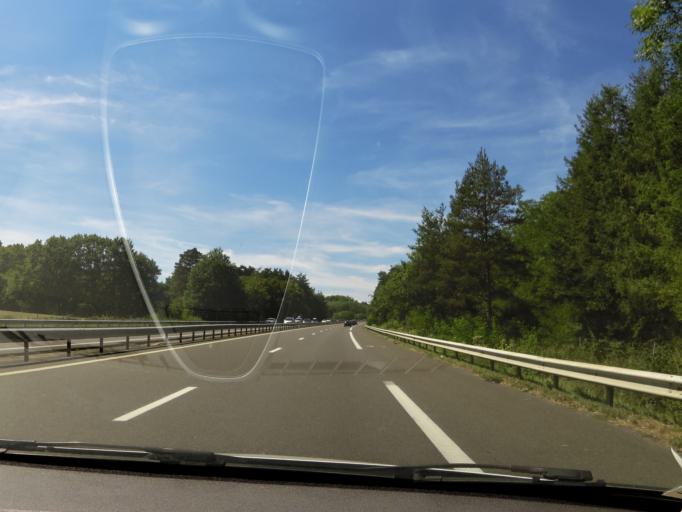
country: FR
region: Auvergne
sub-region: Departement du Puy-de-Dome
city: Orleat
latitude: 45.8507
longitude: 3.4486
